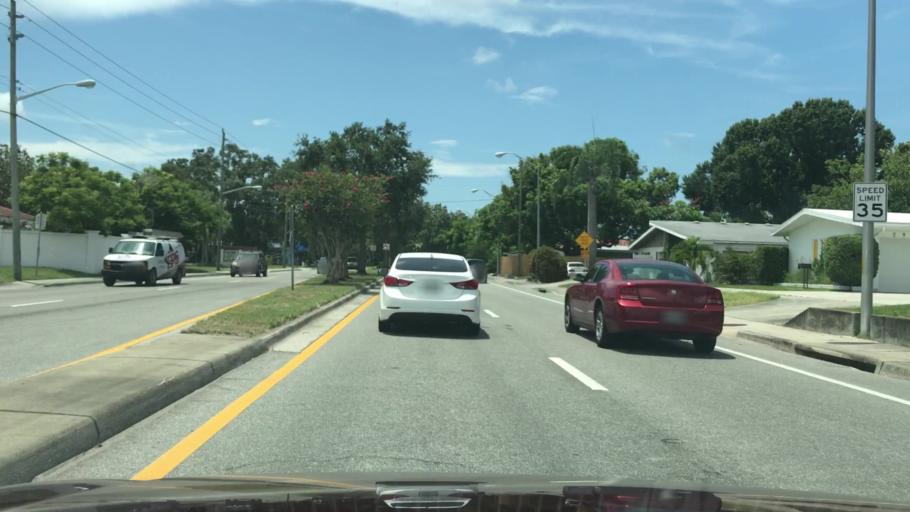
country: US
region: Florida
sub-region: Sarasota County
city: Southgate
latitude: 27.3078
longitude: -82.5142
